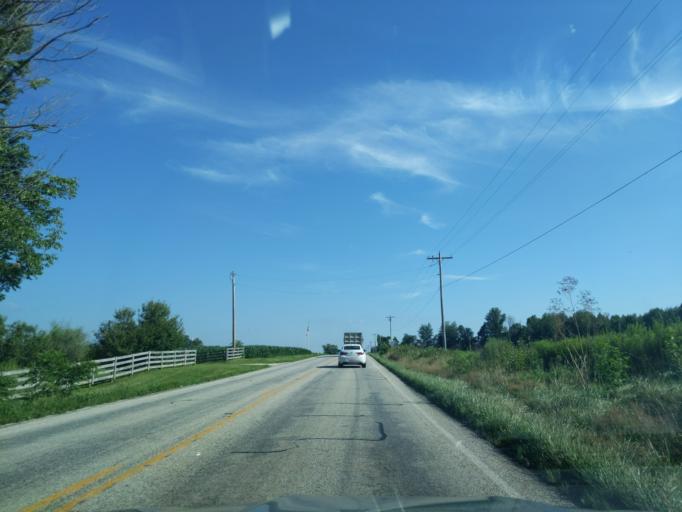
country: US
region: Indiana
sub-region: Ripley County
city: Versailles
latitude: 39.0850
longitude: -85.2741
